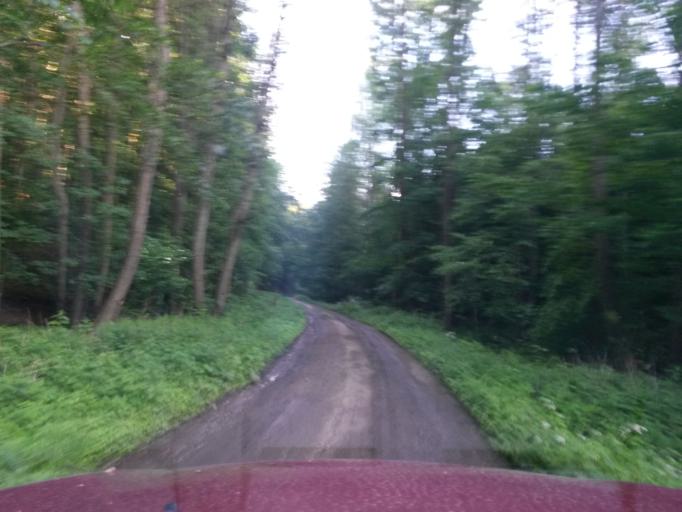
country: SK
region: Kosicky
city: Moldava nad Bodvou
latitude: 48.7393
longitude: 21.0642
